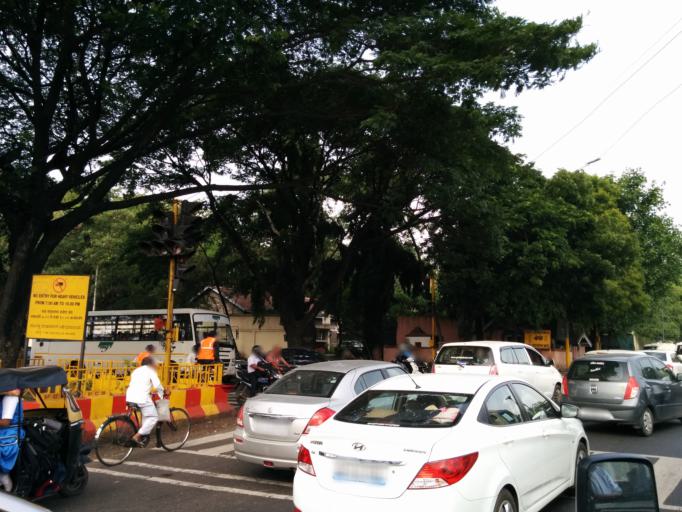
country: IN
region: Maharashtra
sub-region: Pune Division
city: Pune
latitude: 18.5065
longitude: 73.8986
